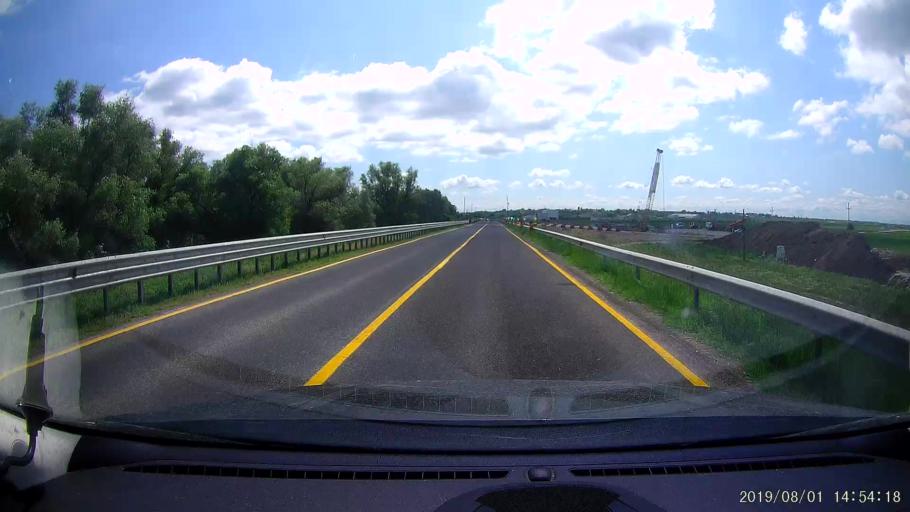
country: RO
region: Braila
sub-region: Municipiul Braila
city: Braila
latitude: 45.3200
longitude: 27.9909
